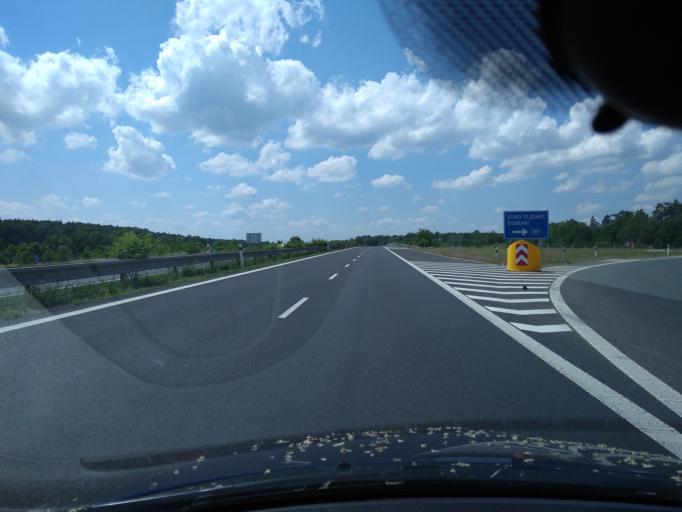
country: CZ
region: Plzensky
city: Chlumcany
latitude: 49.6619
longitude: 13.3446
